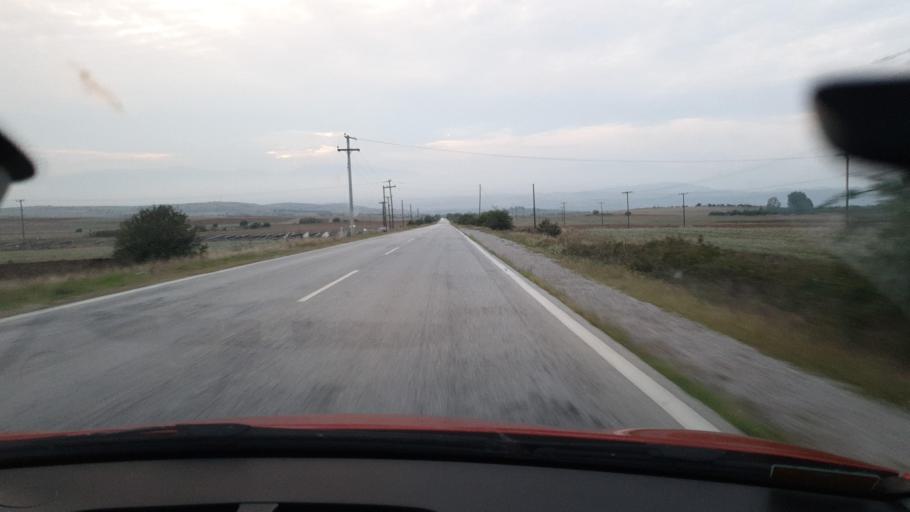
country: GR
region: Central Macedonia
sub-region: Nomos Kilkis
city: Polykastro
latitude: 41.0063
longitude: 22.7028
